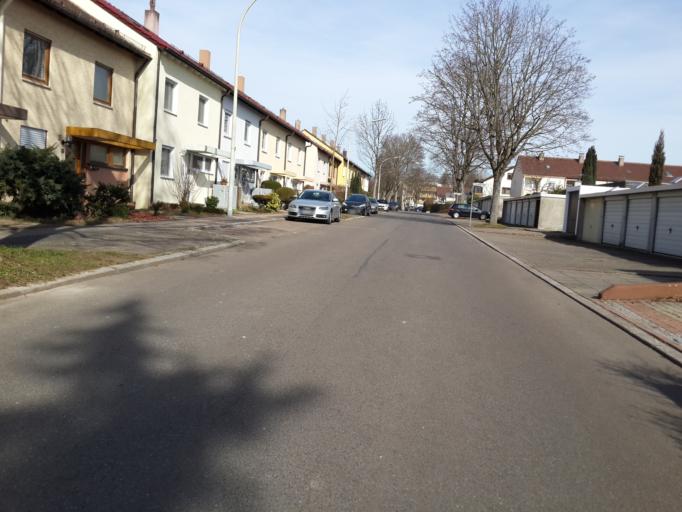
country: DE
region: Baden-Wuerttemberg
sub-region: Regierungsbezirk Stuttgart
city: Heilbronn
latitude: 49.1471
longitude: 9.1764
